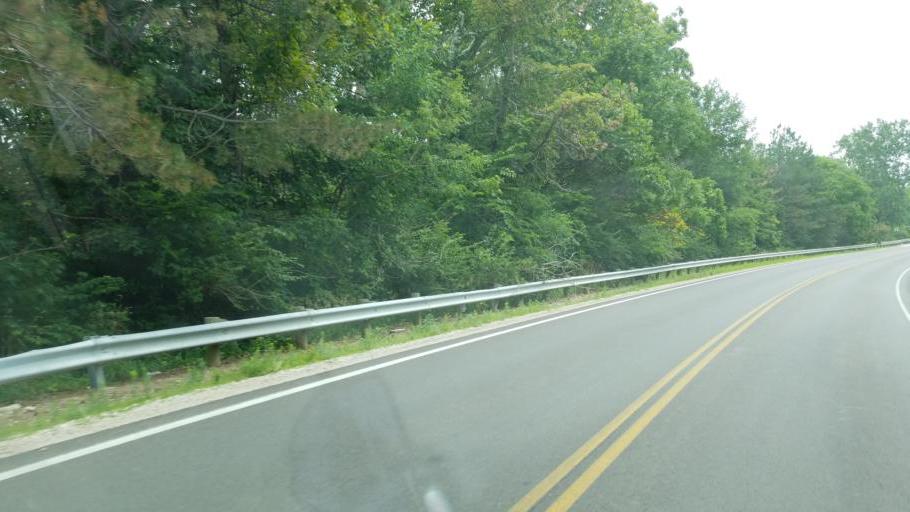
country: US
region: Ohio
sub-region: Madison County
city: Plain City
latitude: 40.0413
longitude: -83.2544
